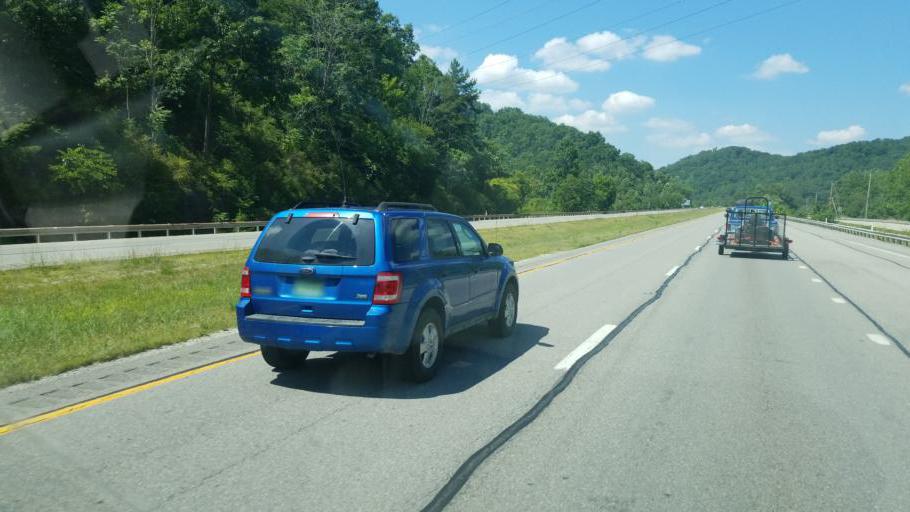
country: US
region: West Virginia
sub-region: Kanawha County
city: Sissonville
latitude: 38.5488
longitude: -81.6346
